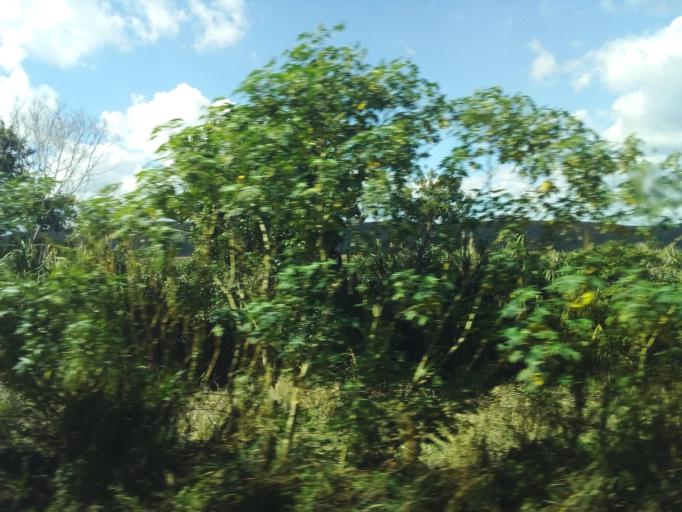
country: BR
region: Minas Gerais
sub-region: Governador Valadares
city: Governador Valadares
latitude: -18.8686
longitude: -41.7708
